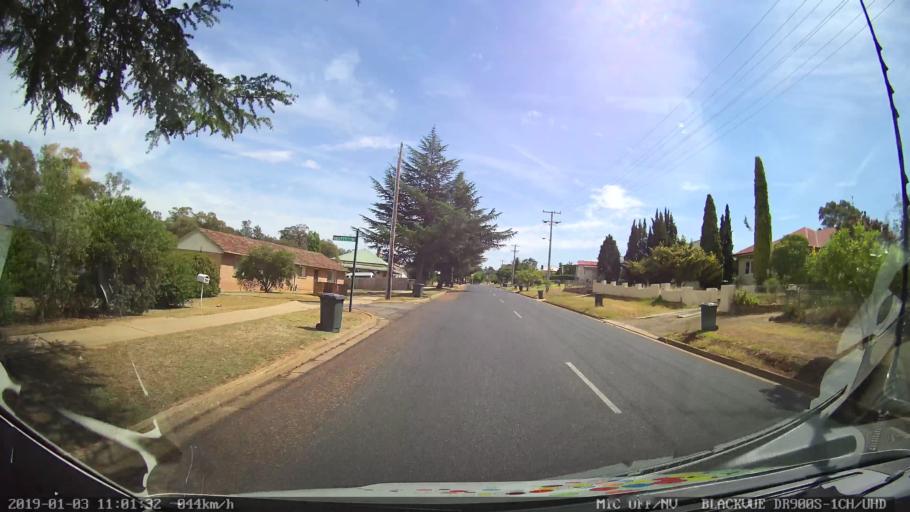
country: AU
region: New South Wales
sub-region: Young
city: Young
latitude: -34.3048
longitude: 148.2994
